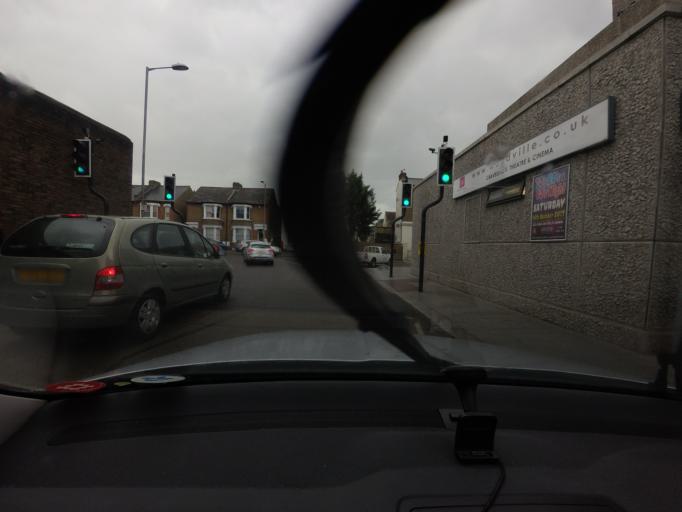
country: GB
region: England
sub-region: Kent
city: Gravesend
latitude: 51.4396
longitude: 0.3683
